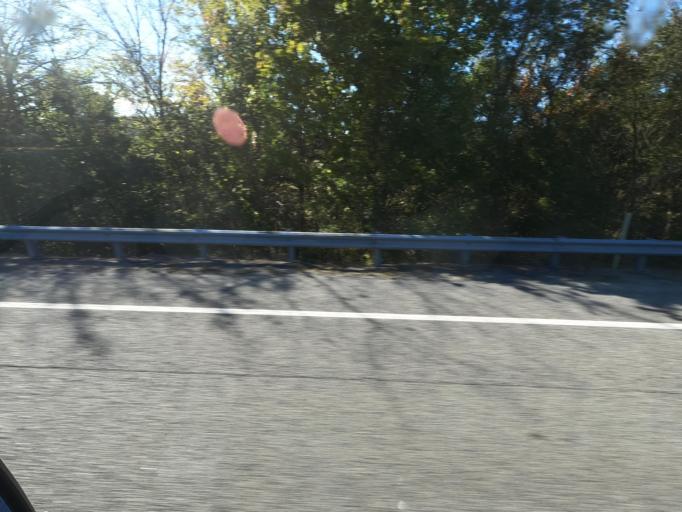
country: US
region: Alabama
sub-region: Limestone County
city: Ardmore
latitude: 35.0099
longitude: -86.8797
